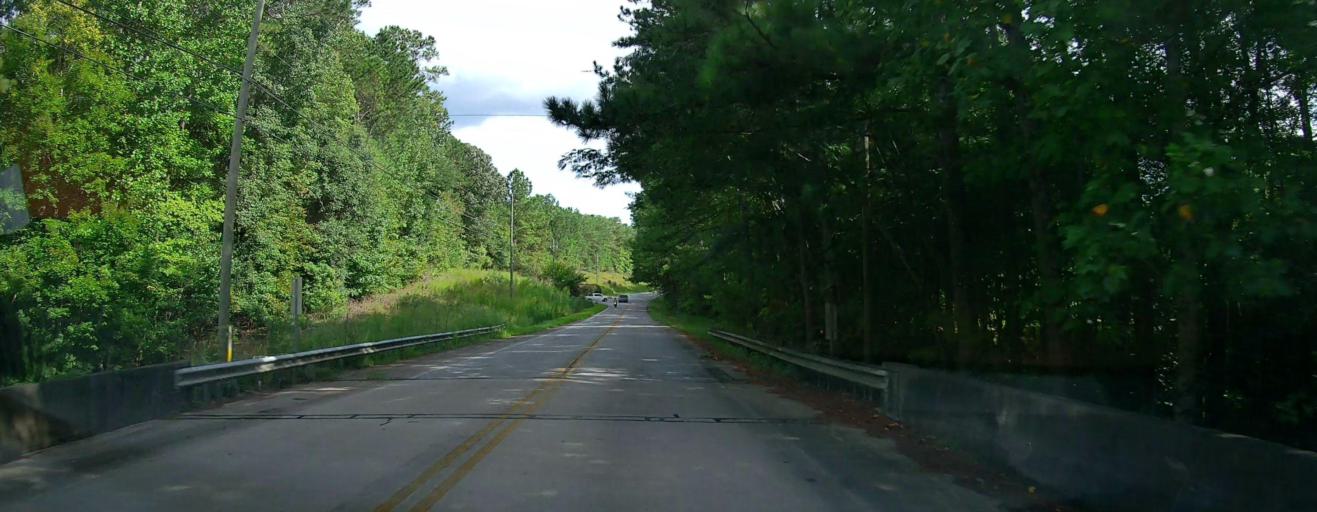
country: US
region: Alabama
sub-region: Russell County
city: Phenix City
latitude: 32.5794
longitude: -84.9724
